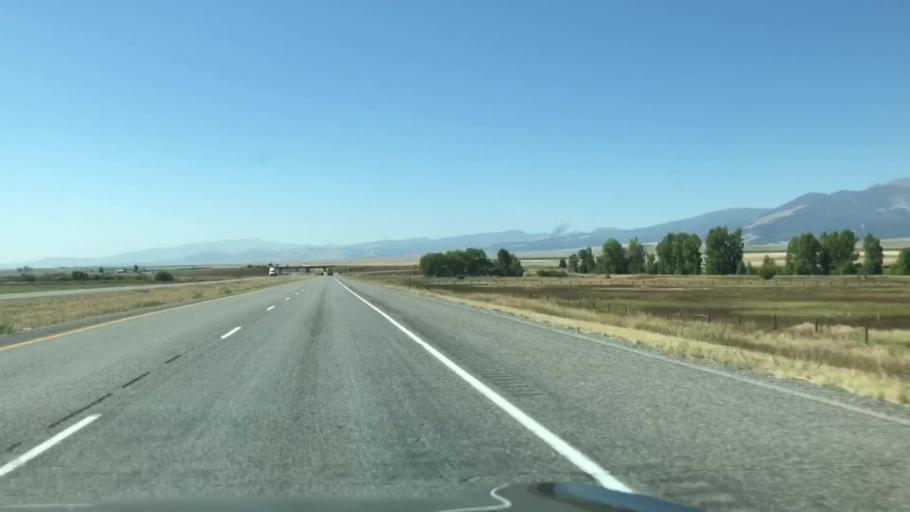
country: US
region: Montana
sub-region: Powell County
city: Deer Lodge
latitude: 46.3805
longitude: -112.7309
